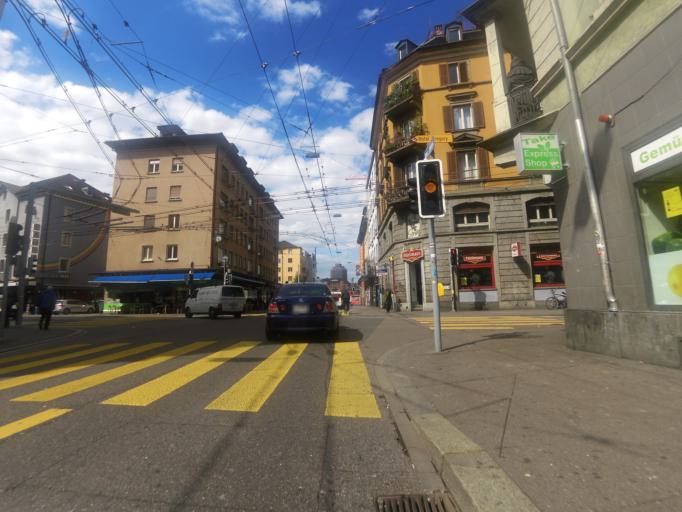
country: CH
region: Zurich
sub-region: Bezirk Zuerich
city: Zuerich (Kreis 4) / Langstrasse
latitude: 47.3795
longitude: 8.5276
